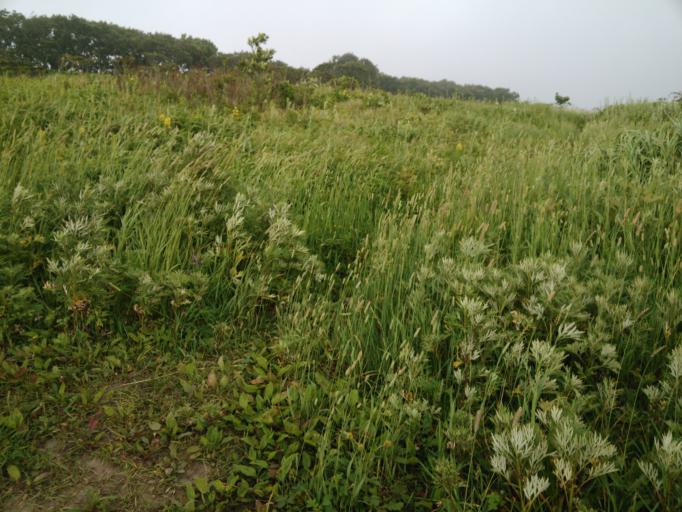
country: RU
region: Primorskiy
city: Vladivostok
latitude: 43.0940
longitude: 131.9882
